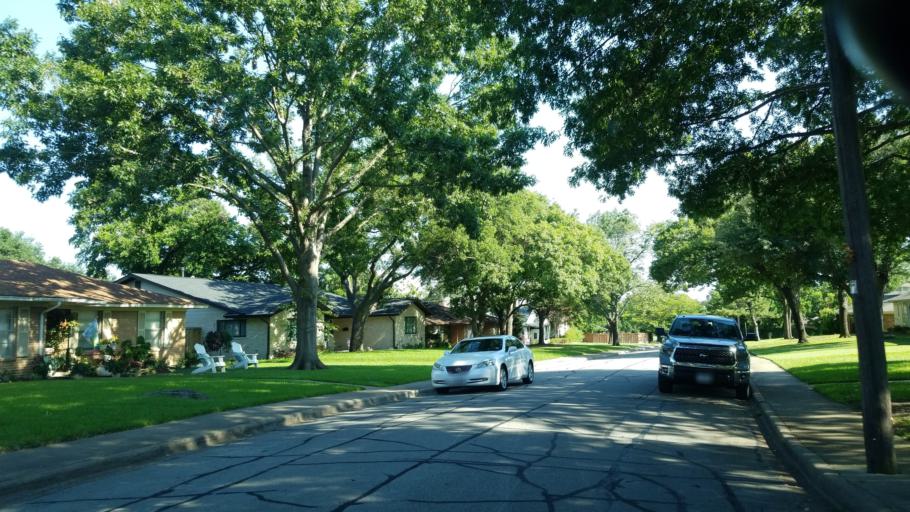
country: US
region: Texas
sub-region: Dallas County
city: Farmers Branch
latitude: 32.9285
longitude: -96.8846
